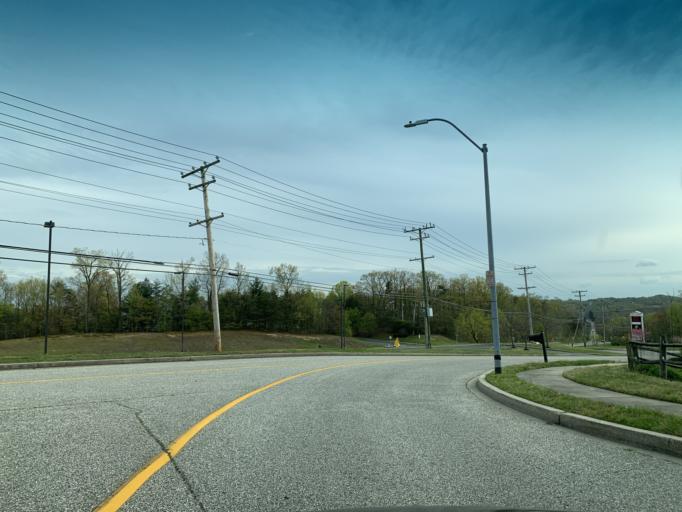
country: US
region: Maryland
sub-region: Harford County
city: Riverside
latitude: 39.4818
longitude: -76.2530
